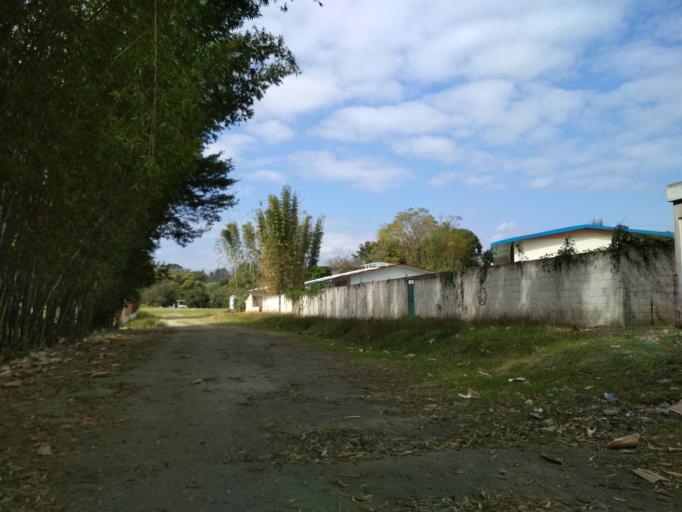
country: MX
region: Veracruz
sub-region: Coatepec
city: Tuzamapan
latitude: 19.3701
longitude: -96.8808
